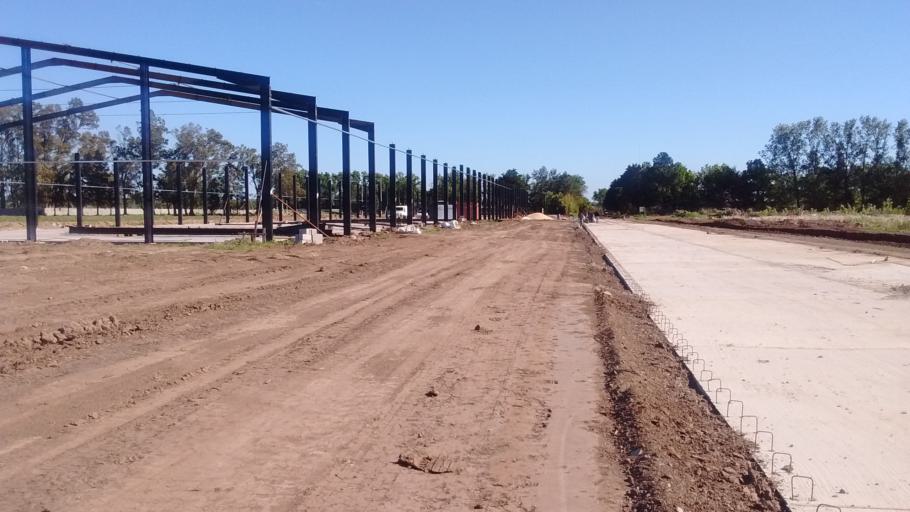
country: AR
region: Santa Fe
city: Perez
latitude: -32.9462
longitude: -60.7384
